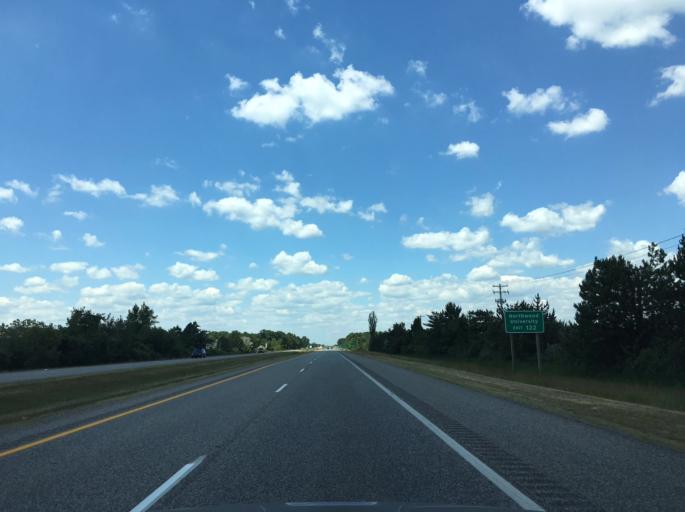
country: US
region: Michigan
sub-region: Midland County
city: Midland
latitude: 43.6560
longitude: -84.2293
